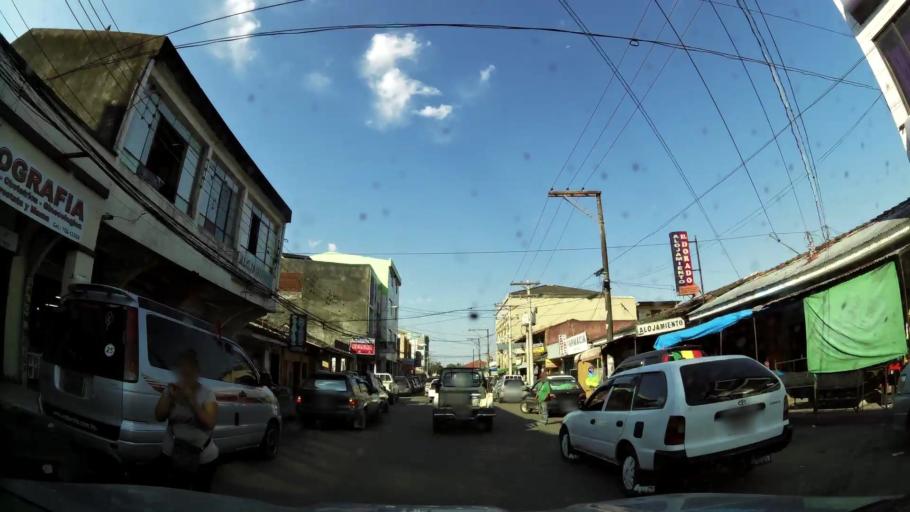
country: BO
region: Santa Cruz
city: Santa Cruz de la Sierra
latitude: -17.7786
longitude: -63.1751
